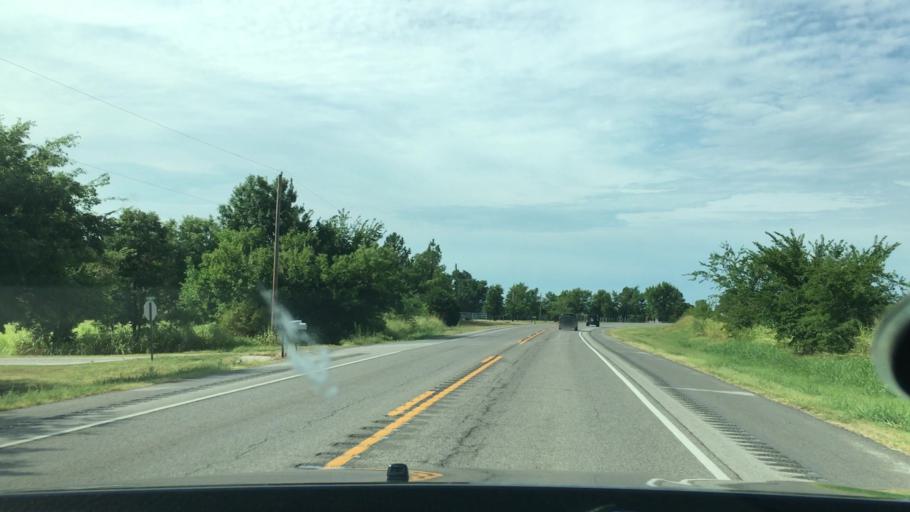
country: US
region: Oklahoma
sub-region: Murray County
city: Sulphur
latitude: 34.5330
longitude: -96.9674
